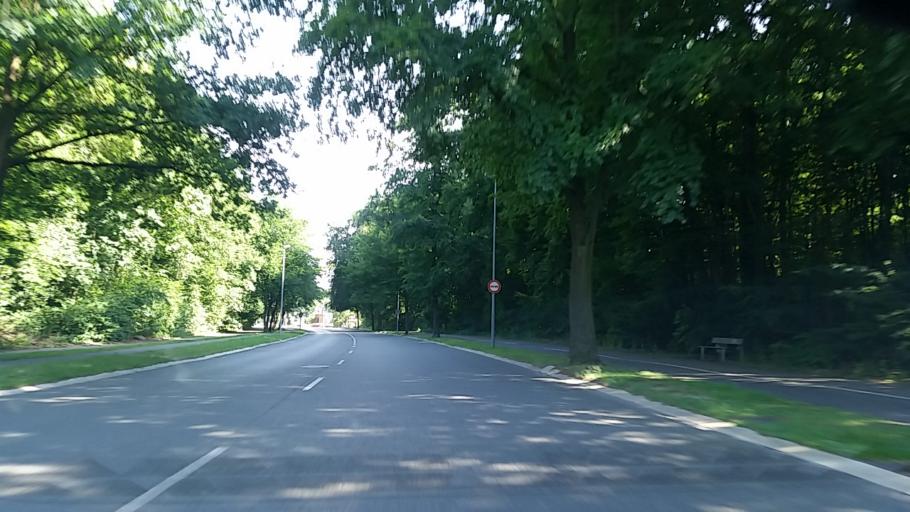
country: DE
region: Lower Saxony
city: Wolfsburg
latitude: 52.4143
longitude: 10.7608
